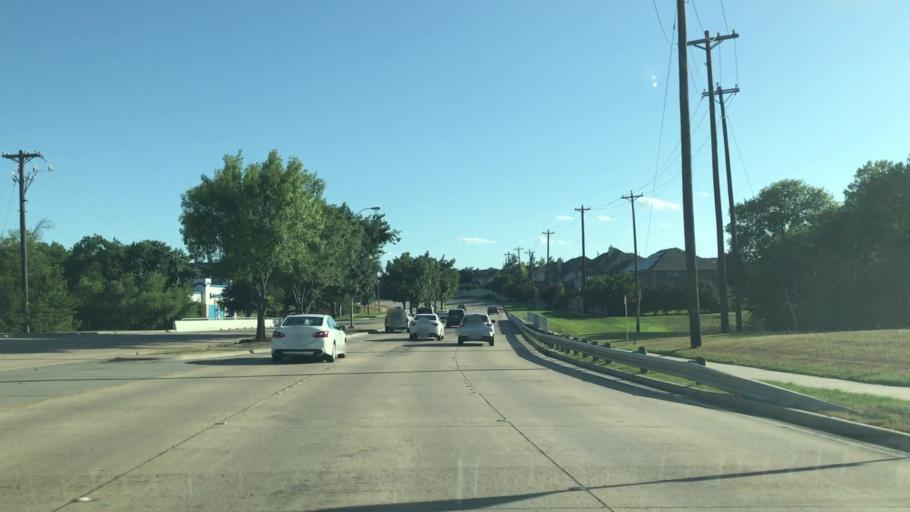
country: US
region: Texas
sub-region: Collin County
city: Allen
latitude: 33.0902
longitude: -96.7343
